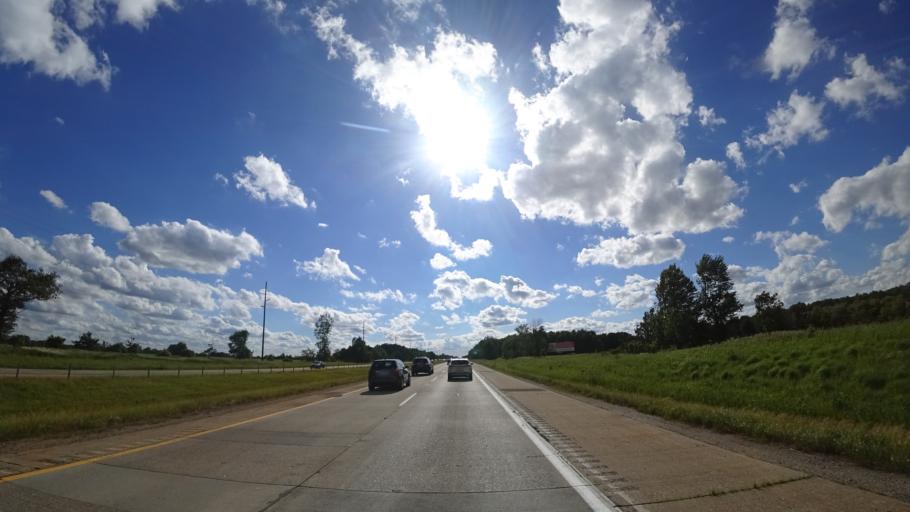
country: US
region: Michigan
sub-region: Ionia County
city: Portland
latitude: 42.8792
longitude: -84.9994
